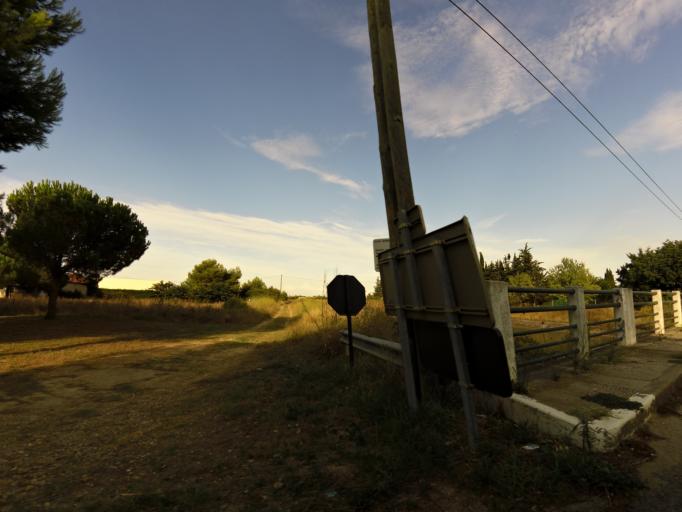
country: FR
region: Languedoc-Roussillon
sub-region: Departement du Gard
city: Gallargues-le-Montueux
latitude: 43.7145
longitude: 4.1709
